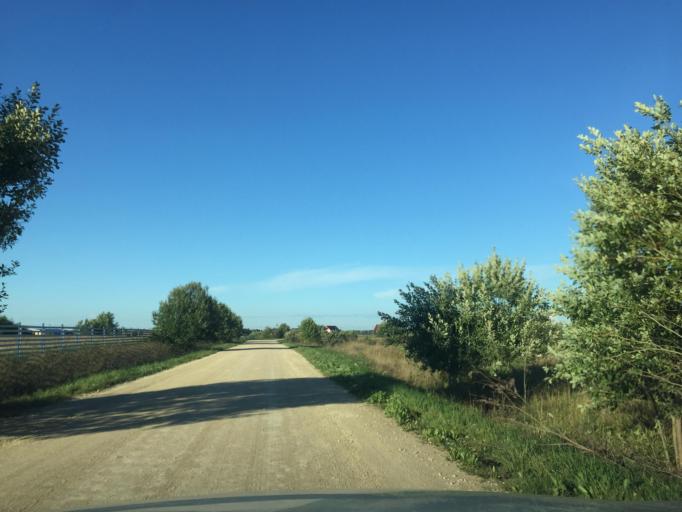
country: RU
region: Leningrad
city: Rozhdestveno
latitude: 59.3316
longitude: 29.9976
